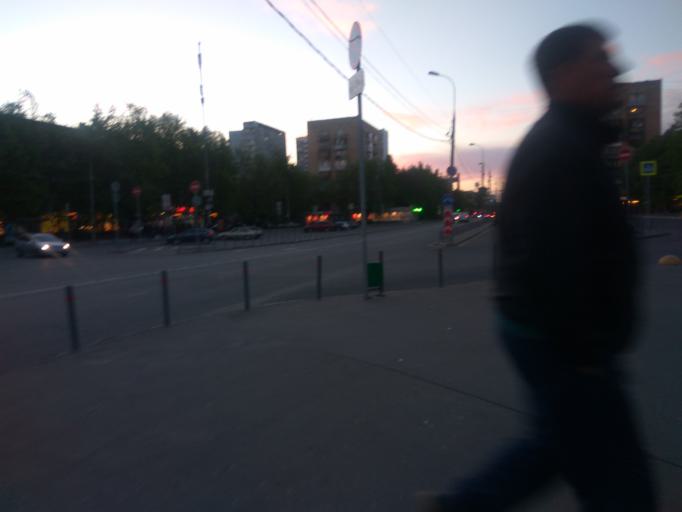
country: RU
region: Moskovskaya
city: Izmaylovo
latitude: 55.7937
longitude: 37.7996
